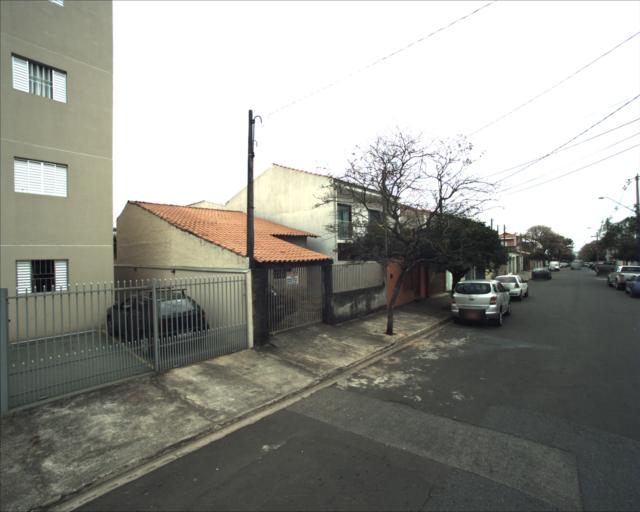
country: BR
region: Sao Paulo
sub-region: Sorocaba
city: Sorocaba
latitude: -23.4982
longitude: -47.5272
